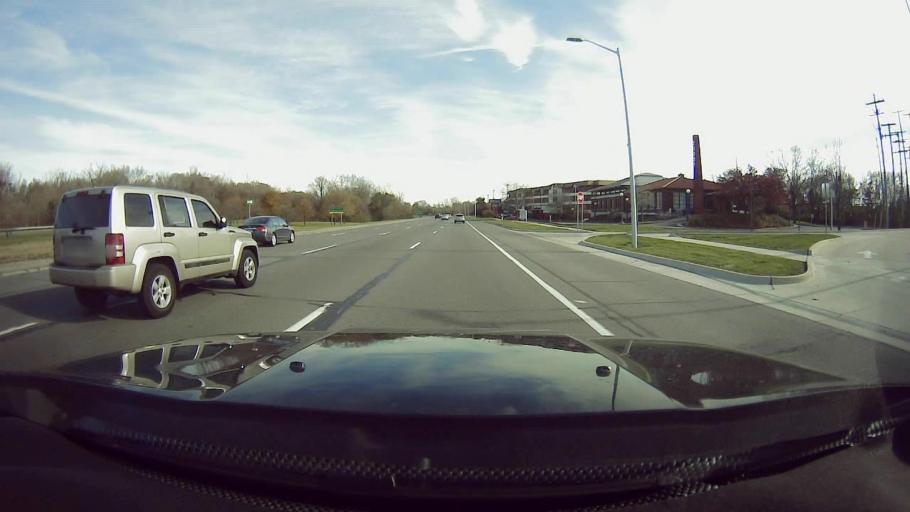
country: US
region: Michigan
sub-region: Wayne County
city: Dearborn Heights
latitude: 42.3079
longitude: -83.2307
